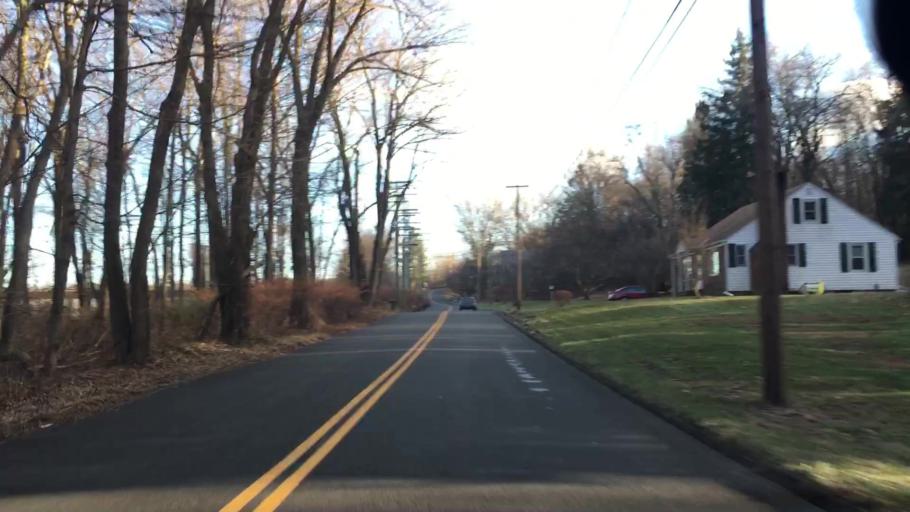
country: US
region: Connecticut
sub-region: Fairfield County
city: Newtown
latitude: 41.4259
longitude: -73.3101
